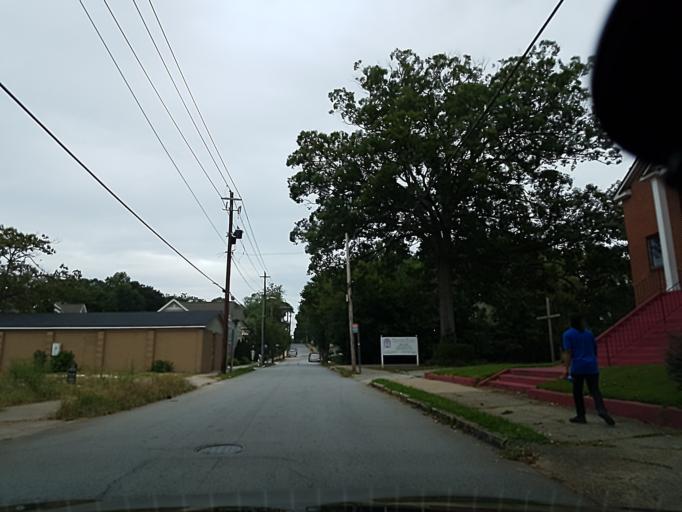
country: US
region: Georgia
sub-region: DeKalb County
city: Druid Hills
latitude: 33.7564
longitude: -84.3387
